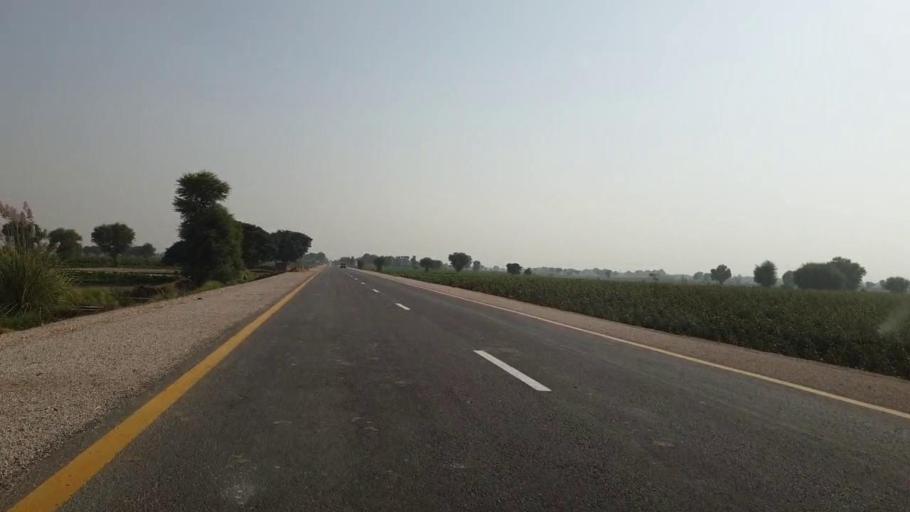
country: PK
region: Sindh
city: Bhan
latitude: 26.5424
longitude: 67.7874
